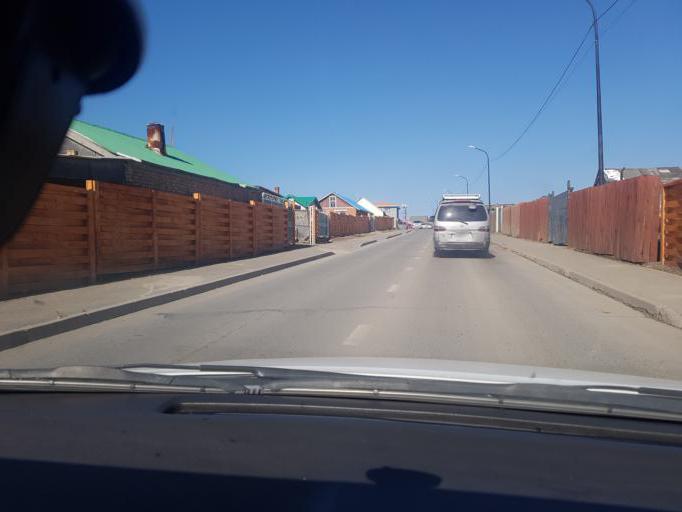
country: MN
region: Ulaanbaatar
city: Ulaanbaatar
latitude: 47.9491
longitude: 106.8673
